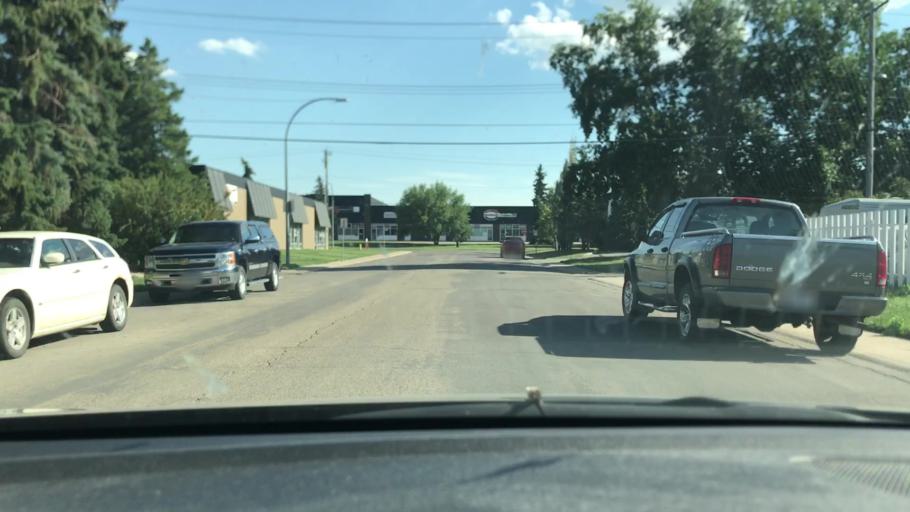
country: CA
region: Alberta
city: Edmonton
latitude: 53.5191
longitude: -113.4228
